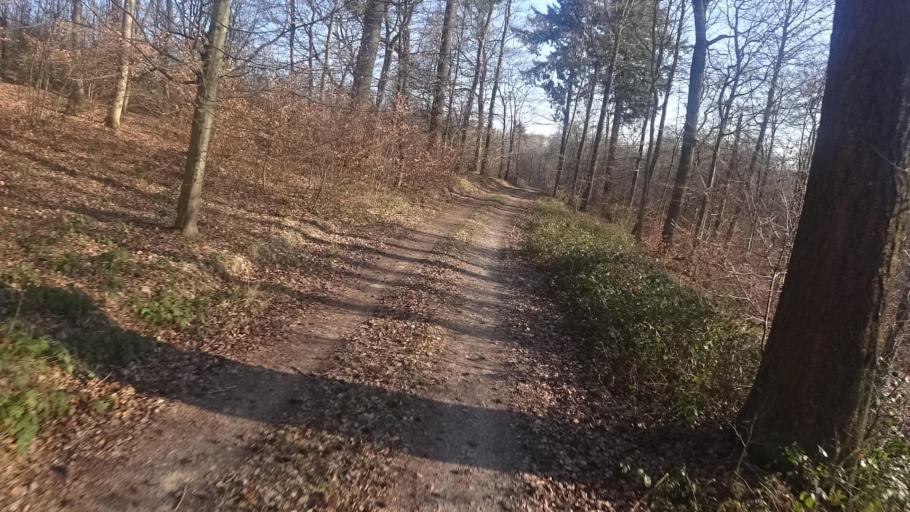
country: DE
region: Rheinland-Pfalz
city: Ney
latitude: 50.2024
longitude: 7.5106
